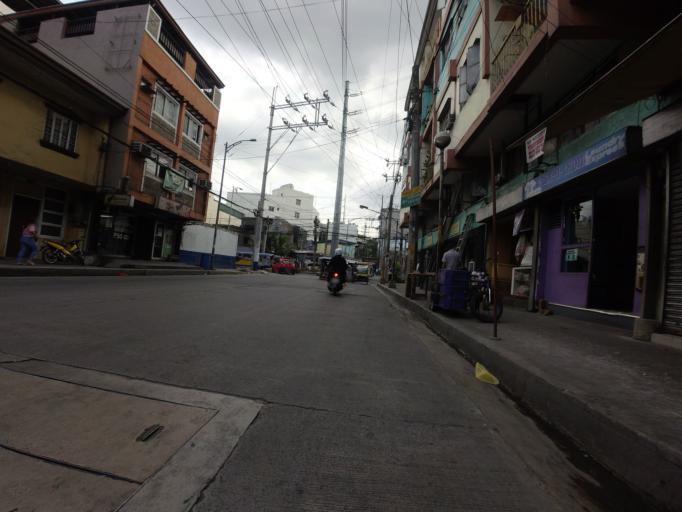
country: PH
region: Metro Manila
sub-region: City of Manila
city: Quiapo
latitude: 14.5790
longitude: 120.9974
